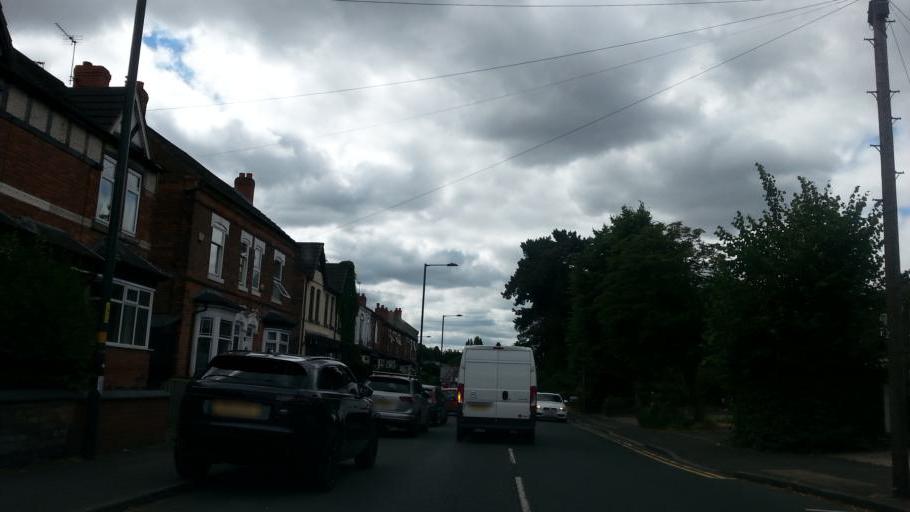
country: GB
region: England
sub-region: City and Borough of Birmingham
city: Sutton Coldfield
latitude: 52.5301
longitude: -1.8414
